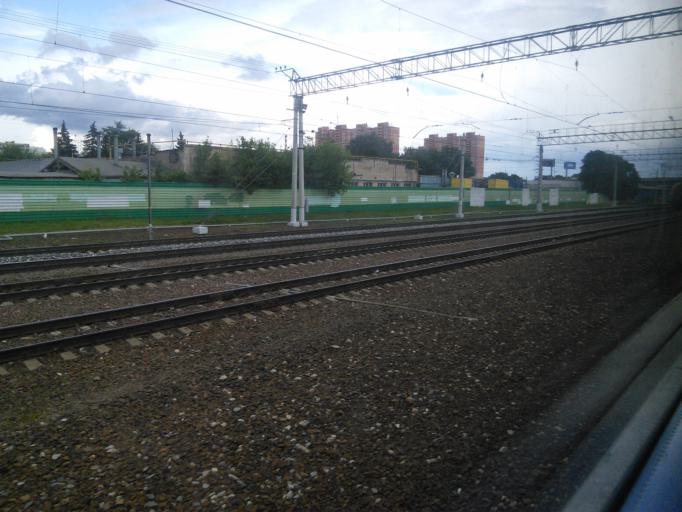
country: RU
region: Moskovskaya
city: Lyubertsy
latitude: 55.6861
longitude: 37.8894
